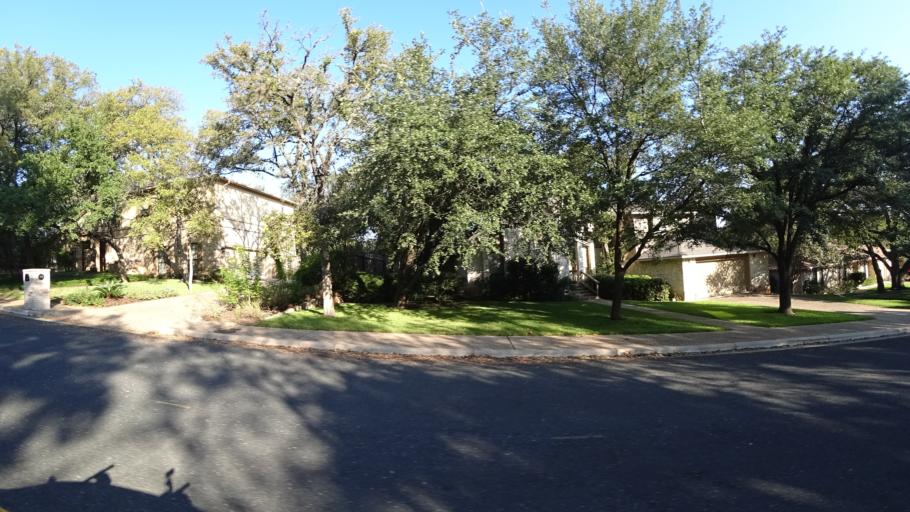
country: US
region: Texas
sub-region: Travis County
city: Rollingwood
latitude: 30.2611
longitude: -97.8045
